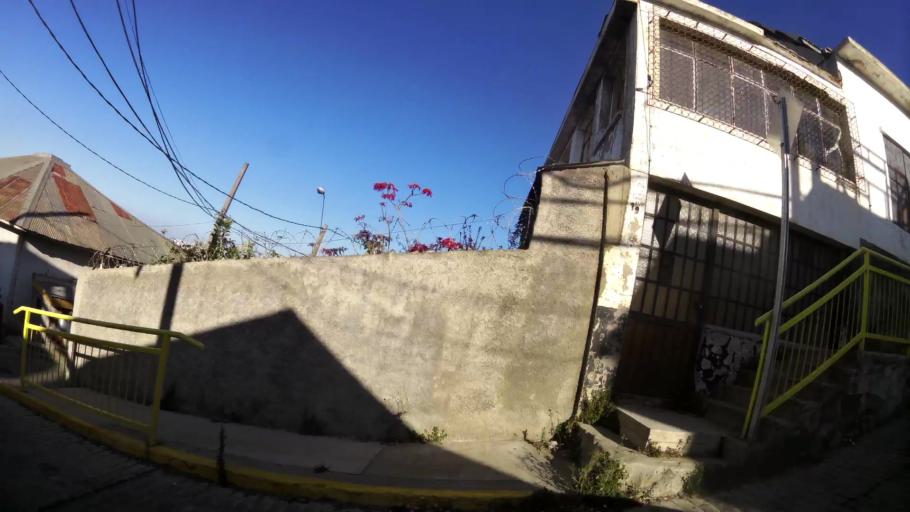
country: CL
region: Valparaiso
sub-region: Provincia de Valparaiso
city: Valparaiso
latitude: -33.0562
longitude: -71.6096
